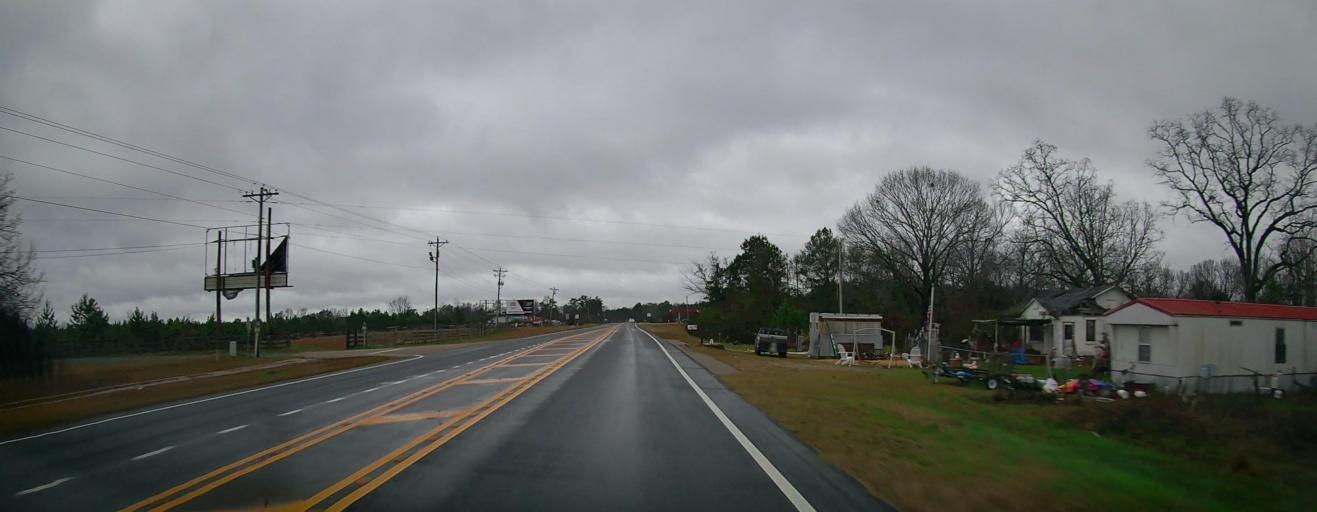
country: US
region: Alabama
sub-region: Chilton County
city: Thorsby
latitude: 32.7911
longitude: -86.9054
